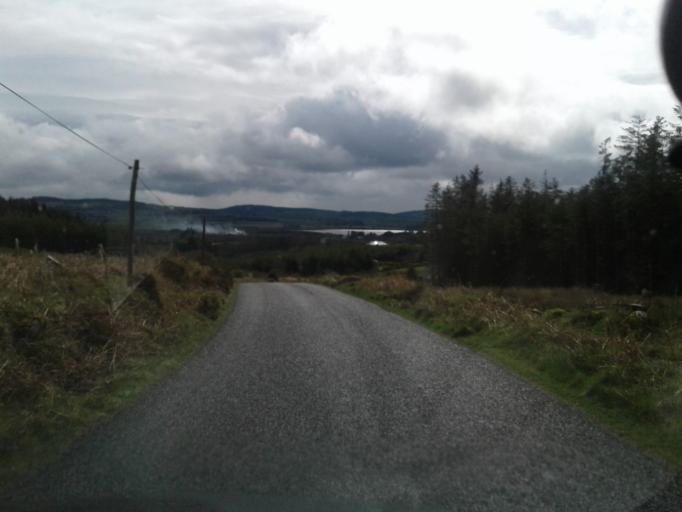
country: IE
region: Leinster
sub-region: Wicklow
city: Enniskerry
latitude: 53.0925
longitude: -6.2411
